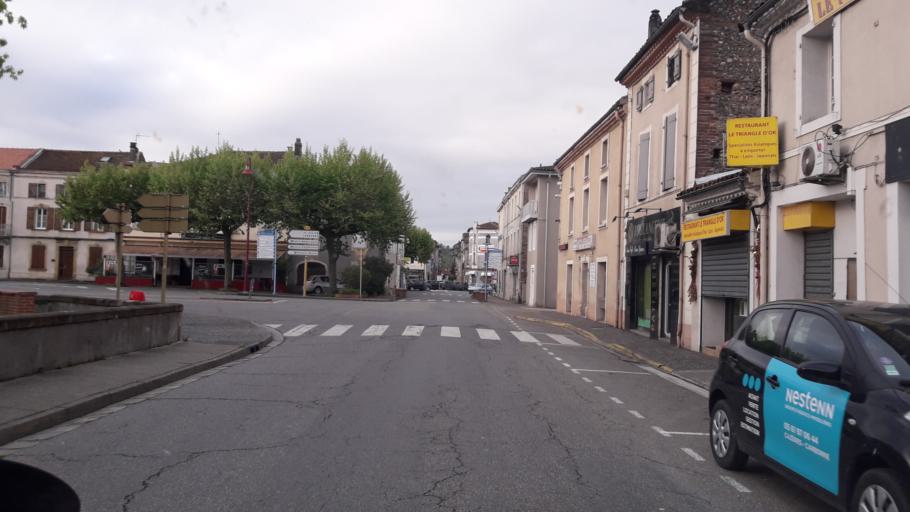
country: FR
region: Midi-Pyrenees
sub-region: Departement de la Haute-Garonne
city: Cazeres
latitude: 43.2083
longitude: 1.0858
